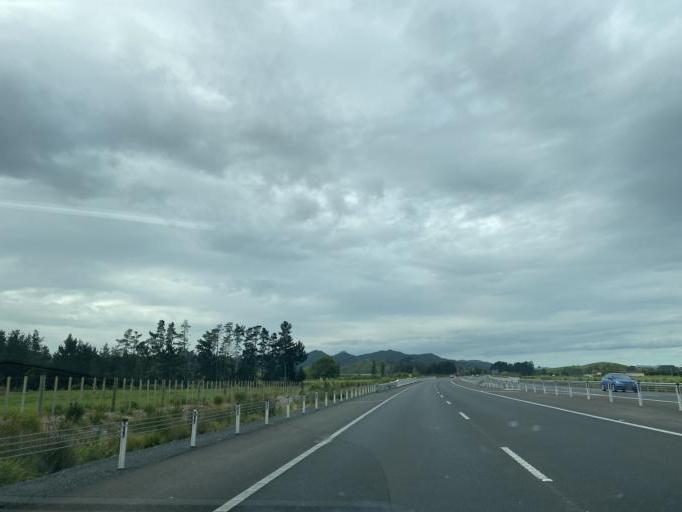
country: NZ
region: Waikato
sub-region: Waikato District
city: Ngaruawahia
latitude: -37.6078
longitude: 175.2047
